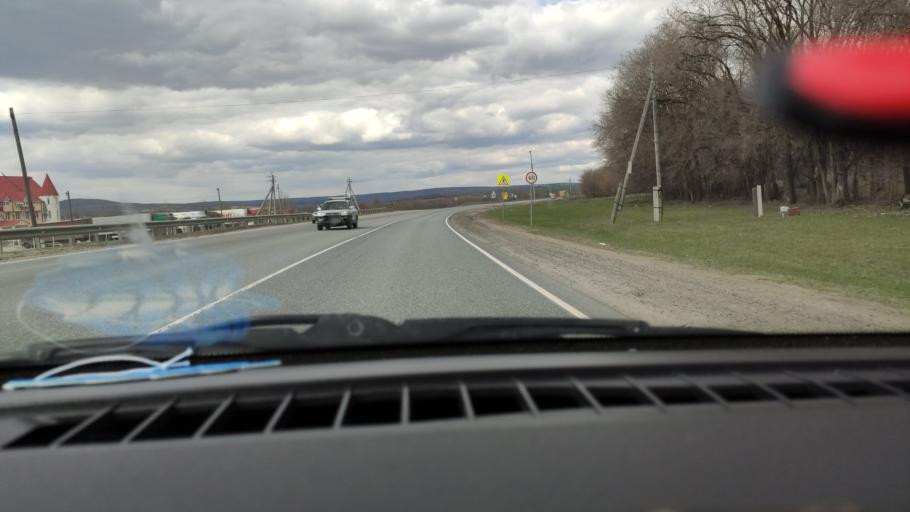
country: RU
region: Saratov
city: Tersa
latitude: 52.0860
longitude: 47.5514
